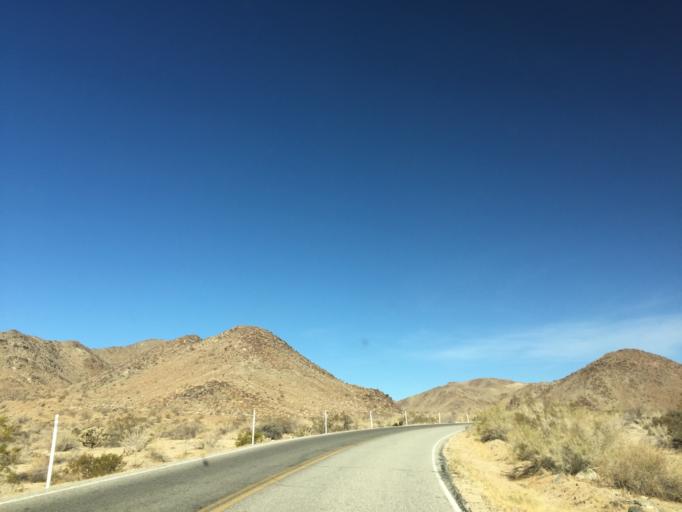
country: US
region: California
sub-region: San Bernardino County
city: Twentynine Palms
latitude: 33.9410
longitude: -115.9718
